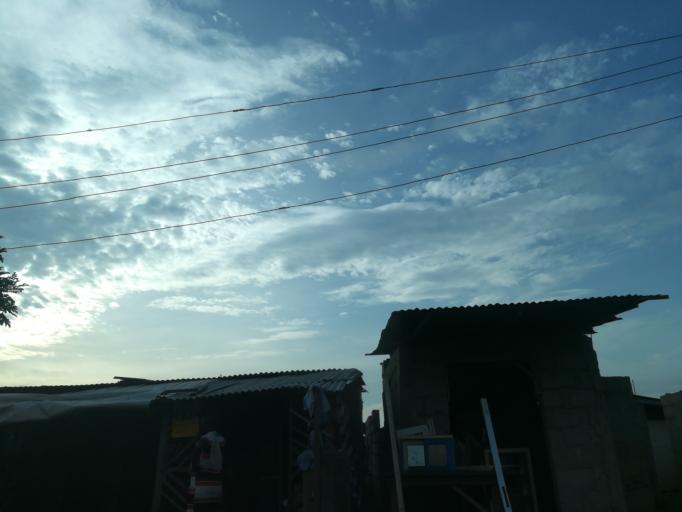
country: NG
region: Lagos
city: Ebute Ikorodu
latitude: 6.6151
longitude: 3.4740
